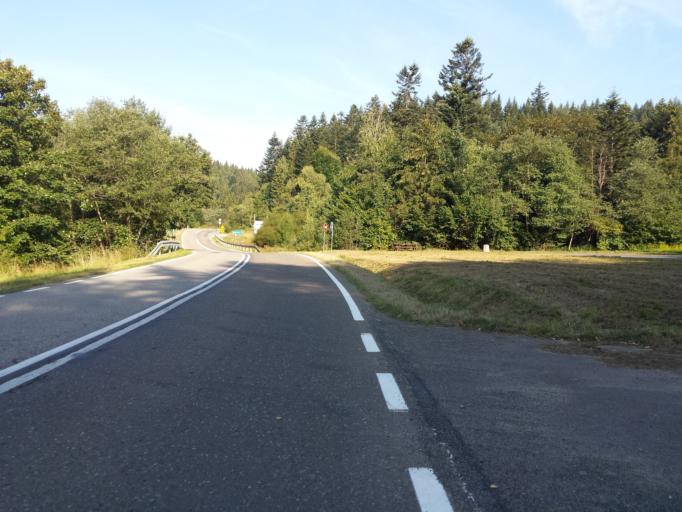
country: PL
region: Subcarpathian Voivodeship
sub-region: Powiat leski
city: Cisna
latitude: 49.2200
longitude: 22.3155
